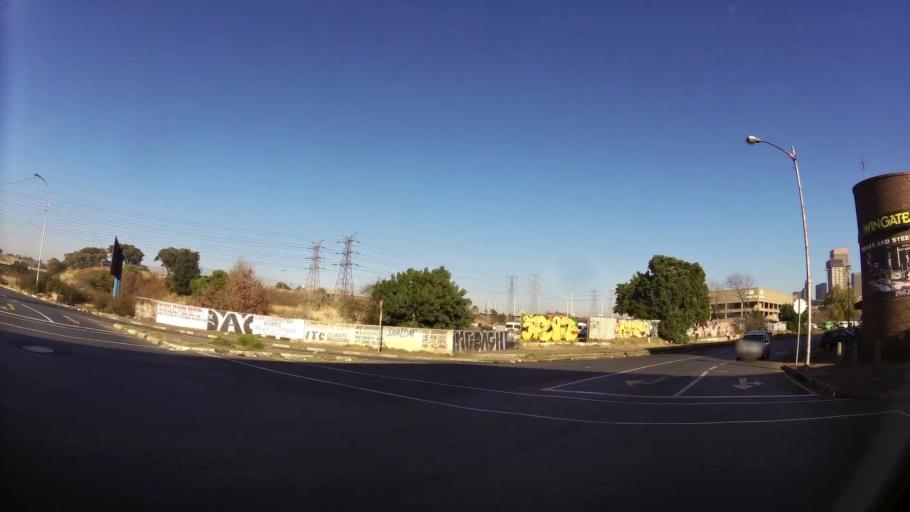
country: ZA
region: Gauteng
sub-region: City of Johannesburg Metropolitan Municipality
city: Johannesburg
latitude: -26.2089
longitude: 28.0612
